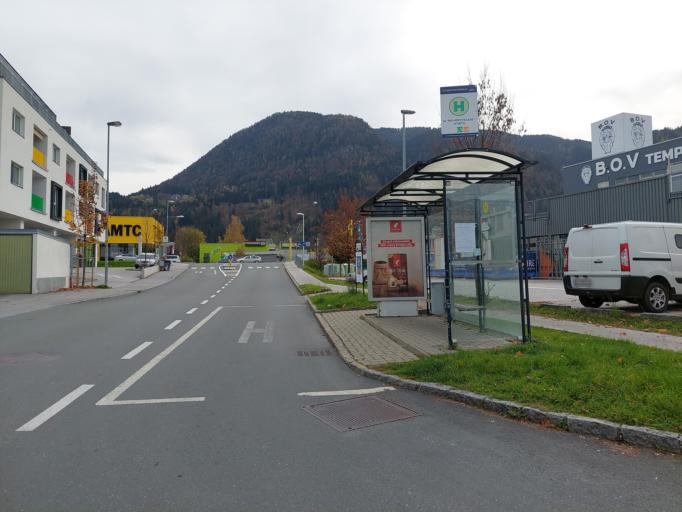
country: AT
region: Tyrol
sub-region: Politischer Bezirk Kufstein
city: Worgl
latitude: 47.4843
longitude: 12.0593
